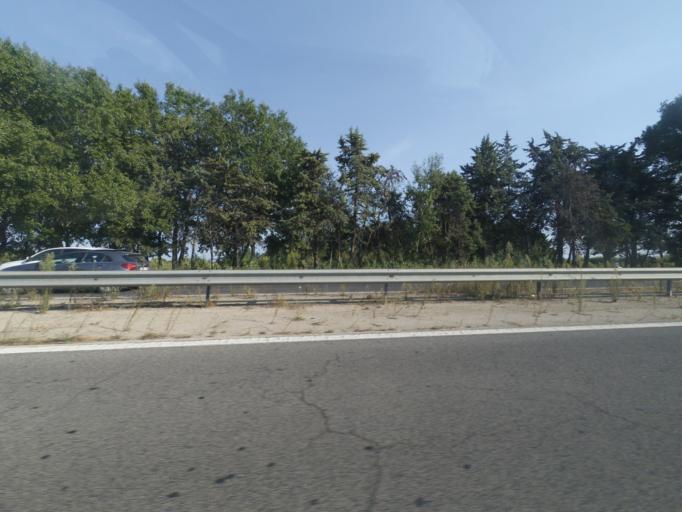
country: FR
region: Languedoc-Roussillon
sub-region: Departement du Gard
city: Le Grau-du-Roi
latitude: 43.5582
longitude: 4.1514
